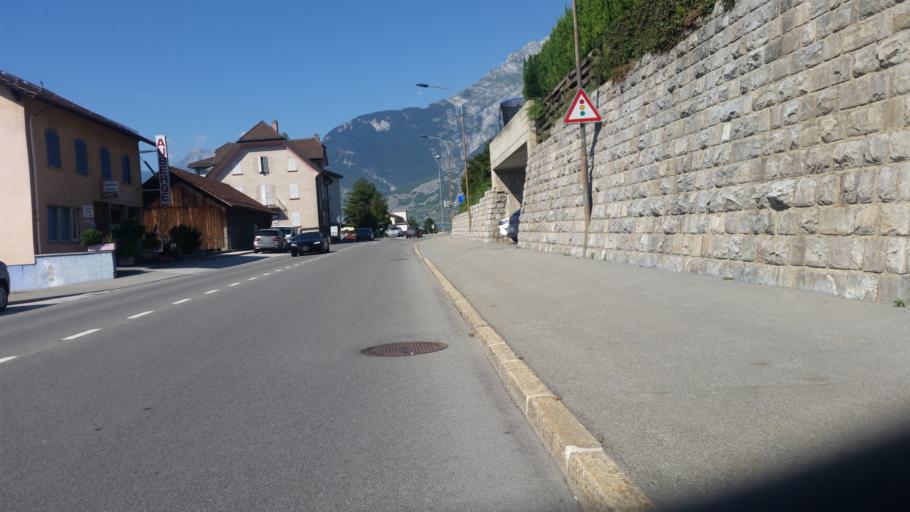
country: CH
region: Valais
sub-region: Conthey District
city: Conthey
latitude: 46.2248
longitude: 7.3149
